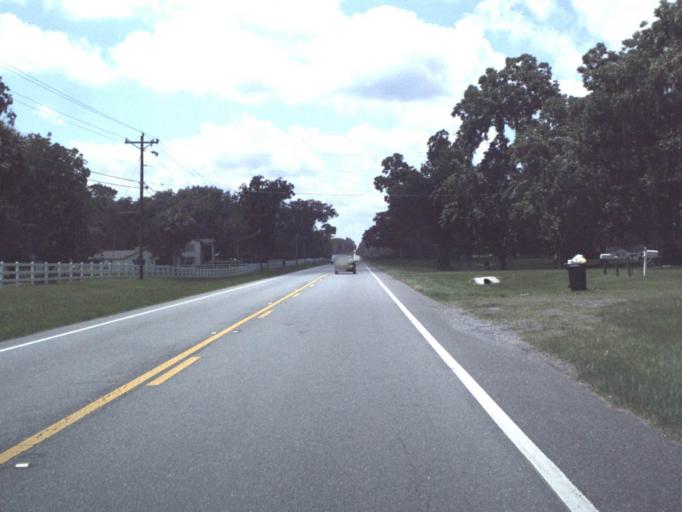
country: US
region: Florida
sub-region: Columbia County
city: Watertown
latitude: 30.0824
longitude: -82.6014
